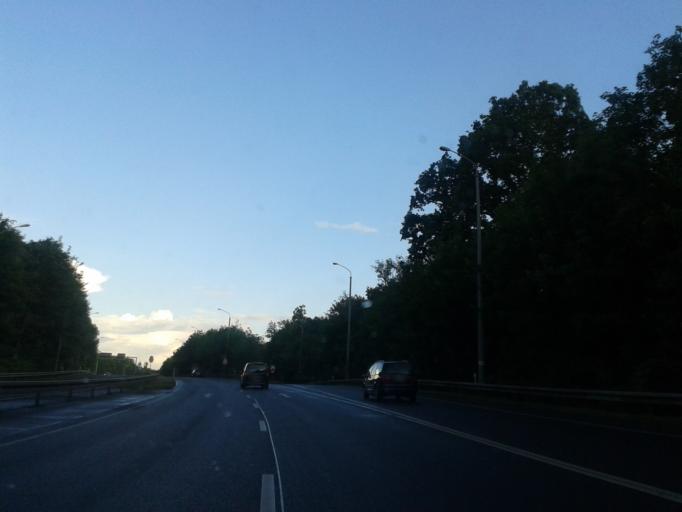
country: DE
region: Saxony
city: Leipzig
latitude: 51.3161
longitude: 12.3598
